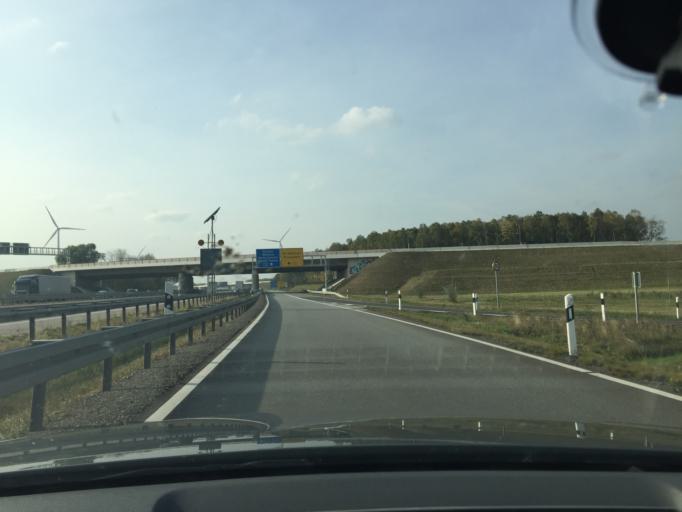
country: DE
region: Brandenburg
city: Ahrensfelde
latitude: 52.6139
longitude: 13.5613
